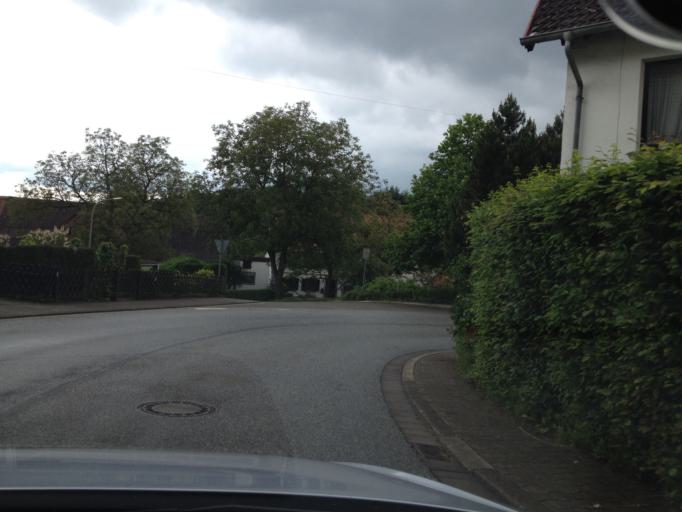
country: DE
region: Saarland
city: Namborn
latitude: 49.5286
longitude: 7.1746
